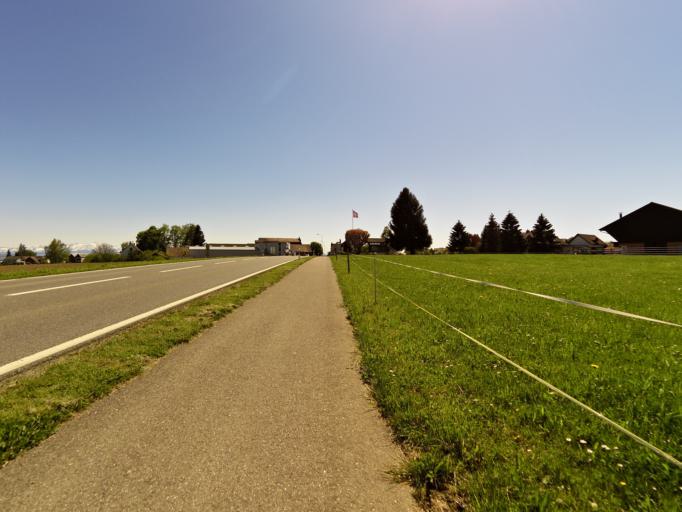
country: CH
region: Thurgau
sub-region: Weinfelden District
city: Berg
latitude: 47.5852
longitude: 9.1692
